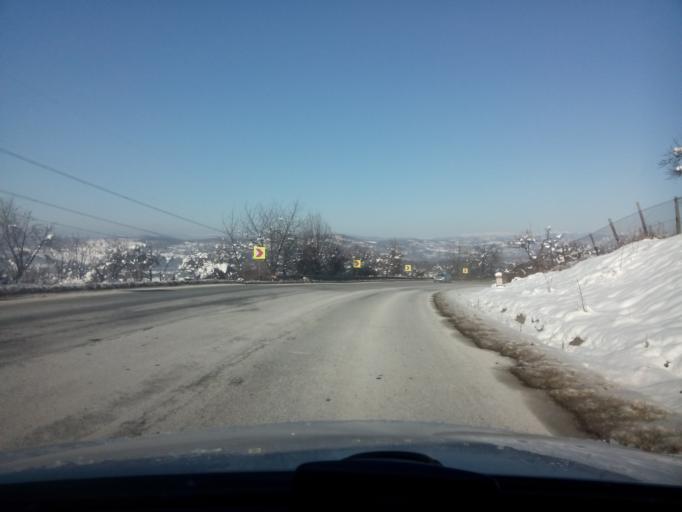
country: RO
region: Arges
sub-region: Comuna Moraresti
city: Moraresti
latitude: 45.0206
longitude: 24.5214
